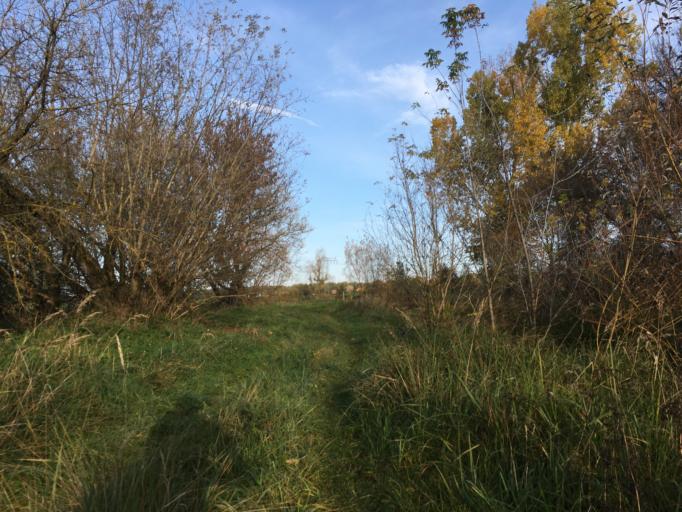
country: DE
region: Berlin
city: Buch
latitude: 52.6729
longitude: 13.4741
